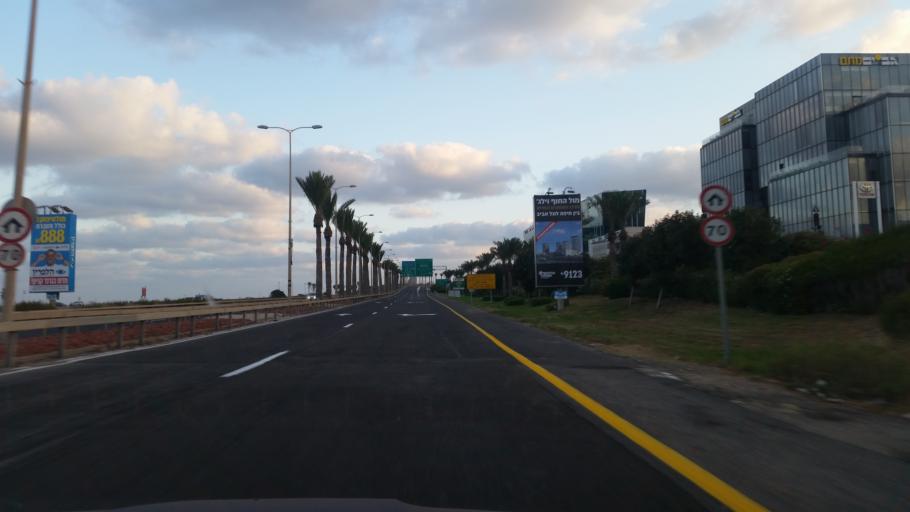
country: IL
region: Haifa
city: Tirat Karmel
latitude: 32.7849
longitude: 34.9566
